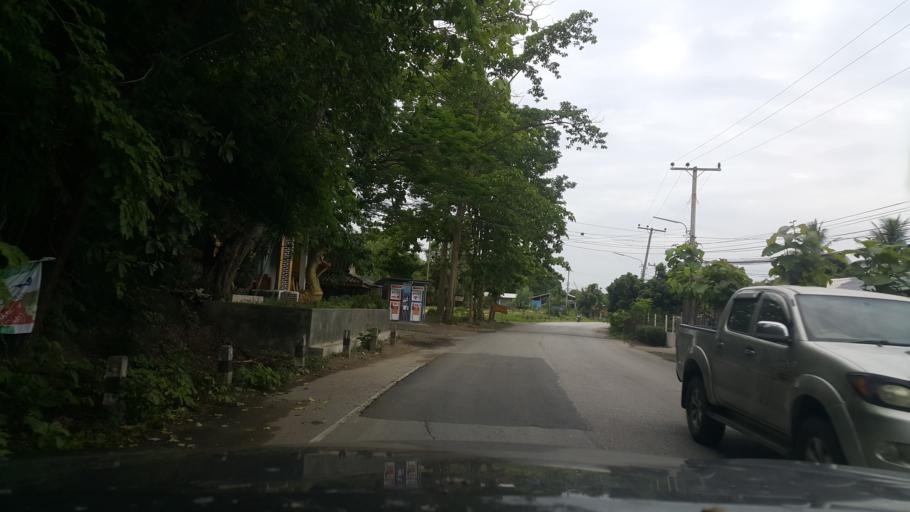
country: TH
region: Chiang Mai
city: San Pa Tong
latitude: 18.6551
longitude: 98.8375
